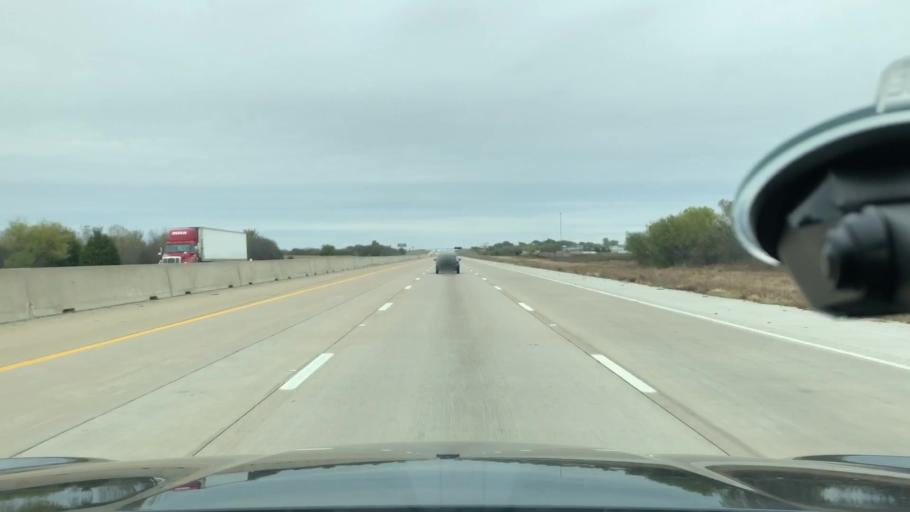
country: US
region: Texas
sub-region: Ellis County
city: Nash
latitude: 32.3038
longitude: -96.8639
